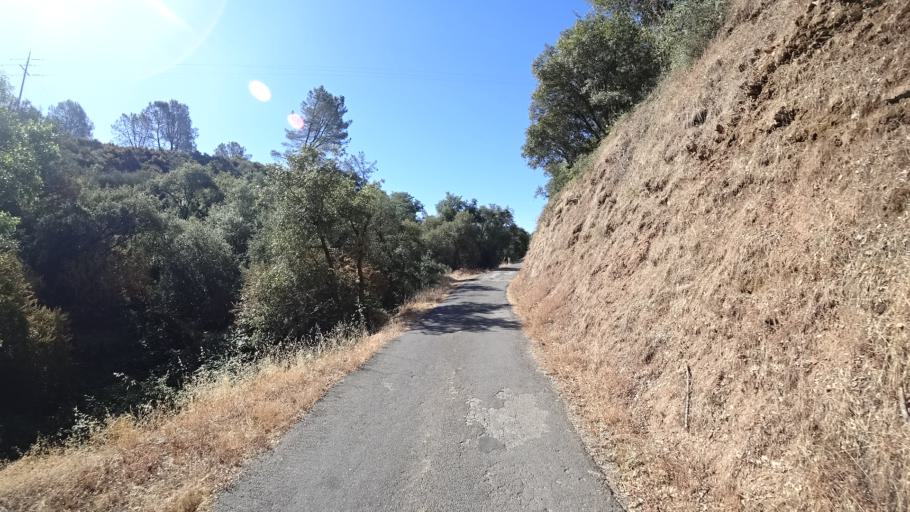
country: US
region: California
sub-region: Amador County
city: Jackson
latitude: 38.2700
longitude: -120.7608
